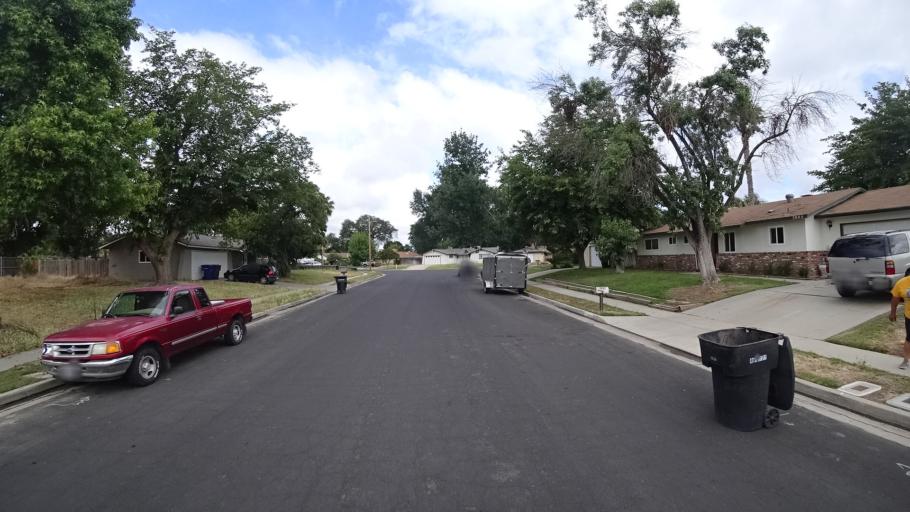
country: US
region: California
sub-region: Kings County
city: Hanford
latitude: 36.3480
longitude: -119.6587
